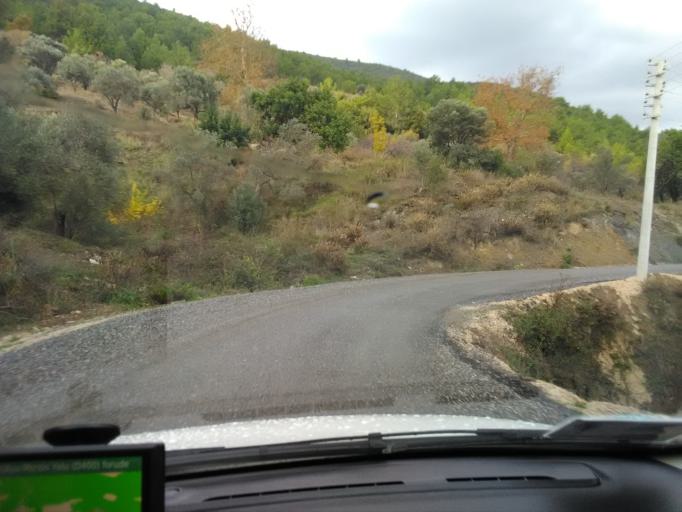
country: TR
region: Antalya
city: Gazipasa
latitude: 36.1619
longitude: 32.4323
